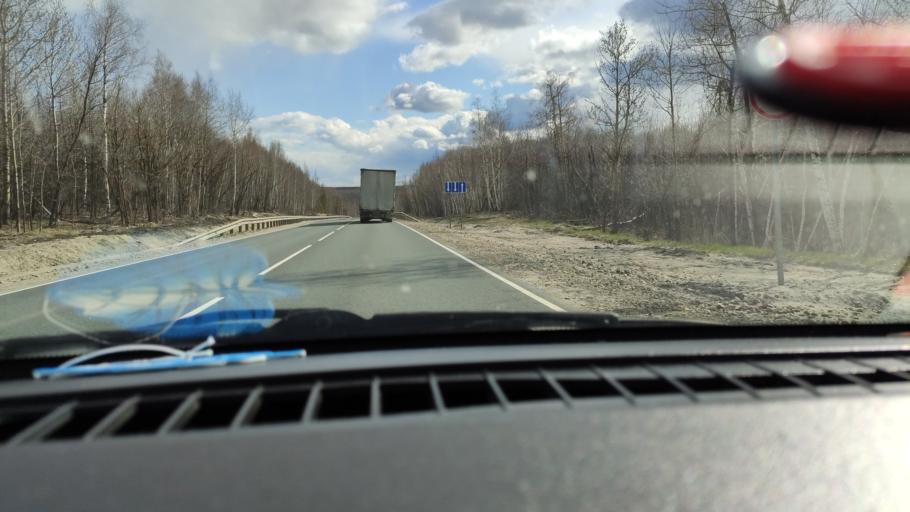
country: RU
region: Saratov
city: Alekseyevka
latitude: 52.4165
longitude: 48.0077
